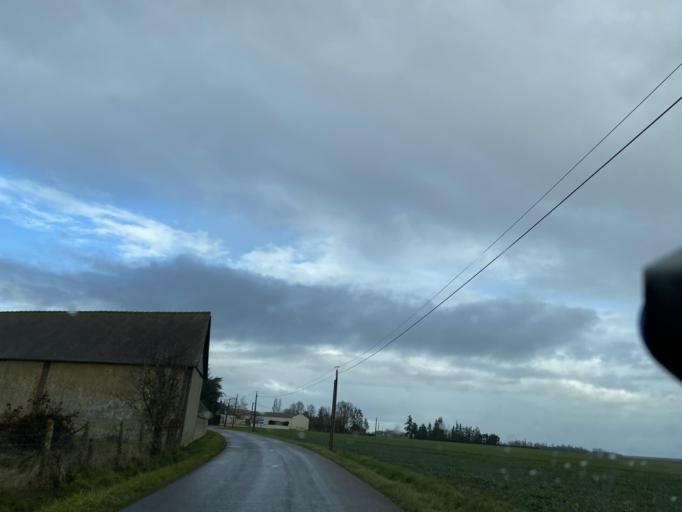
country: FR
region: Haute-Normandie
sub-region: Departement de l'Eure
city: Tillieres-sur-Avre
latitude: 48.7852
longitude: 1.0608
